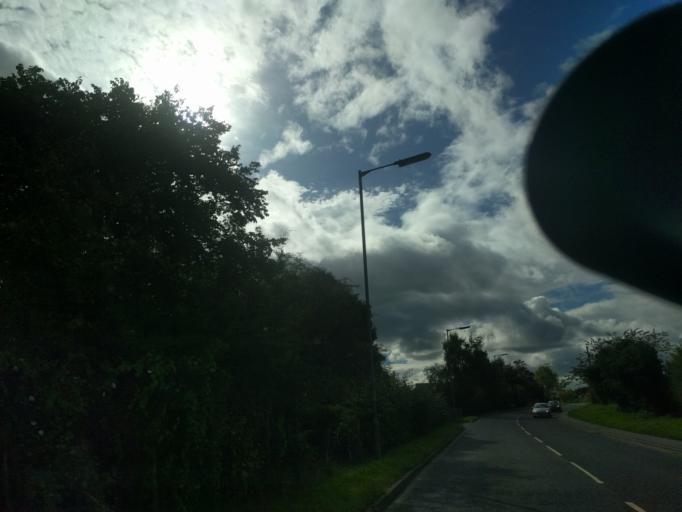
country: GB
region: England
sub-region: North Yorkshire
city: Bedale
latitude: 54.2973
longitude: -1.5728
